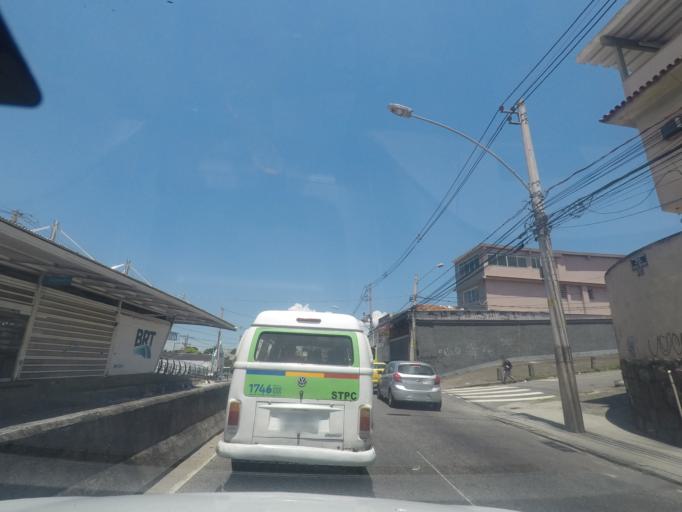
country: BR
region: Rio de Janeiro
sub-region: Duque De Caxias
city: Duque de Caxias
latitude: -22.8420
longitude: -43.2758
